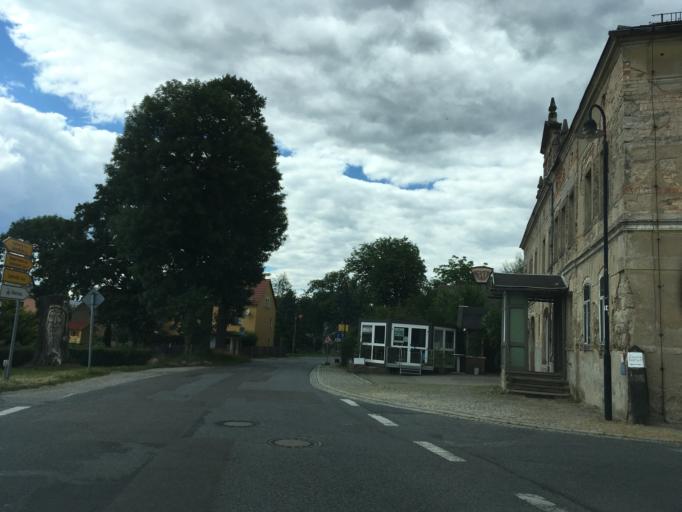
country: DE
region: Saxony
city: Wachau
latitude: 51.1553
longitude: 13.9076
